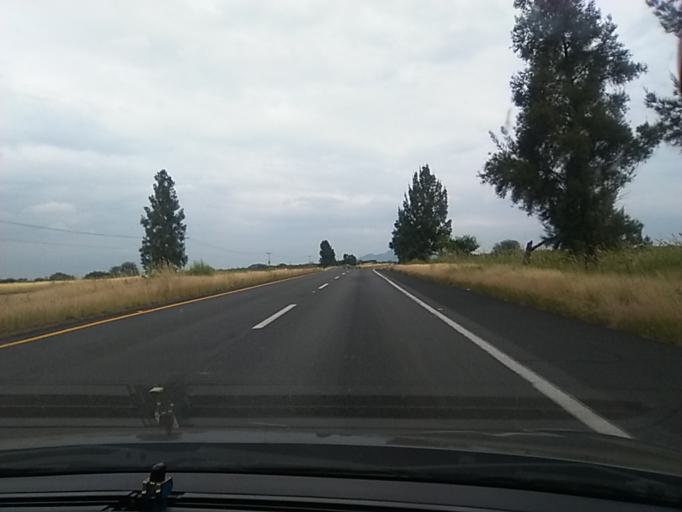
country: MX
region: Michoacan
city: Ecuandureo
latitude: 20.1676
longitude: -102.1346
